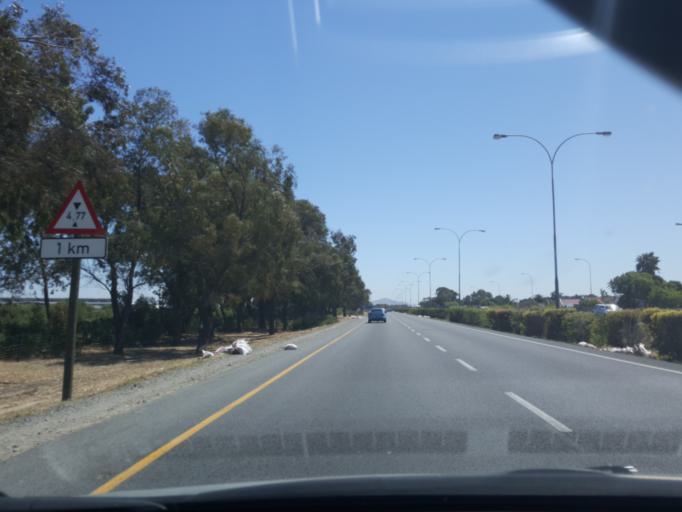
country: ZA
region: Western Cape
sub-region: City of Cape Town
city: Sunset Beach
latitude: -33.8575
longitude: 18.5310
